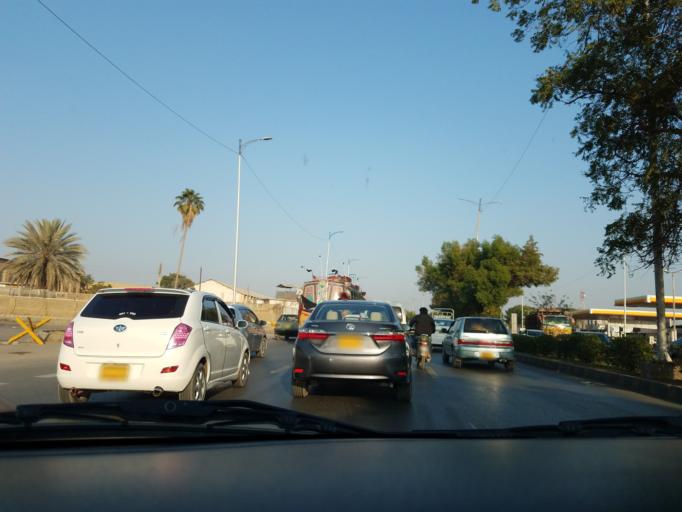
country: PK
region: Sindh
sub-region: Karachi District
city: Karachi
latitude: 24.8860
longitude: 67.1209
